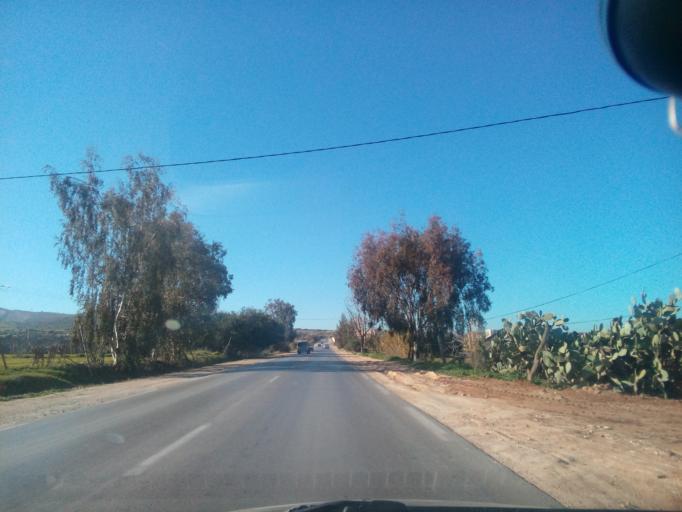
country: DZ
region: Relizane
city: Relizane
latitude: 35.9029
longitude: 0.5218
